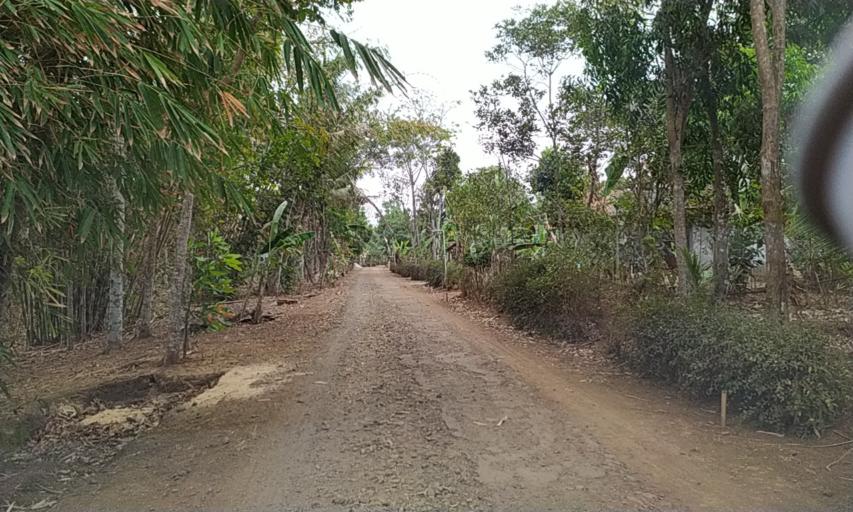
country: ID
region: Central Java
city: Kroya
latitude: -7.6449
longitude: 109.2533
